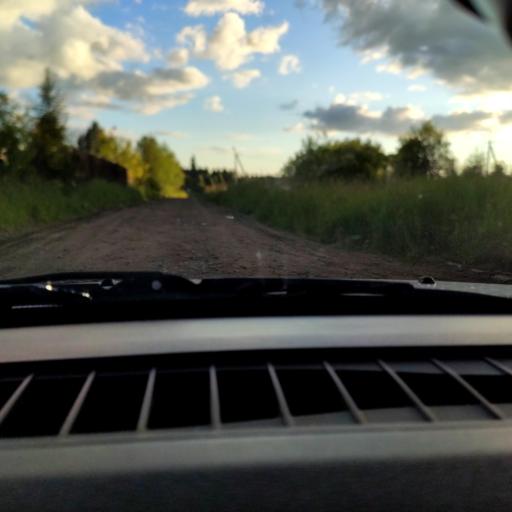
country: RU
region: Perm
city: Polazna
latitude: 58.1911
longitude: 56.4900
